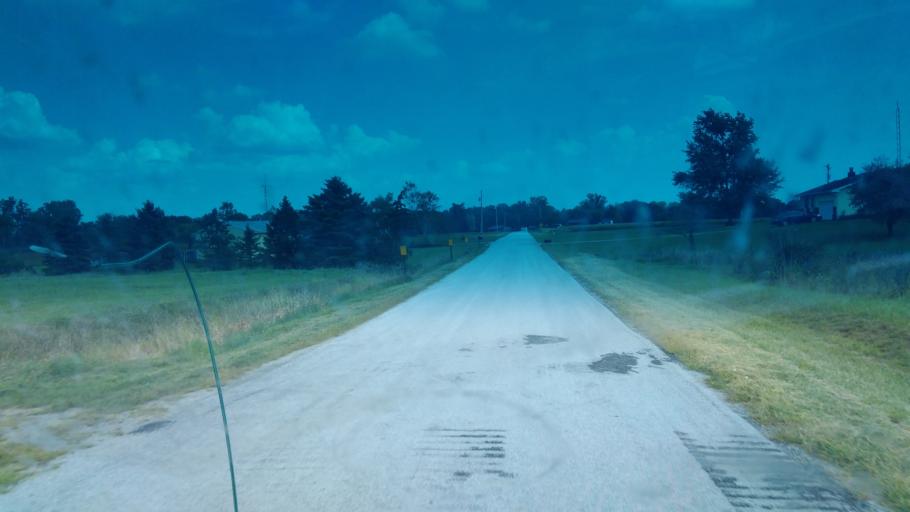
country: US
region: Ohio
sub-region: Hardin County
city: Kenton
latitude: 40.6603
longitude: -83.6784
